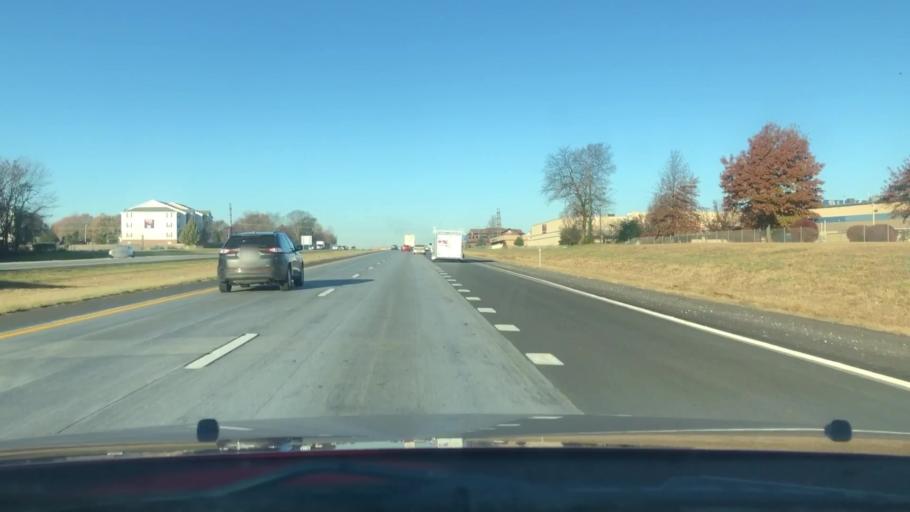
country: US
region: Missouri
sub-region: Greene County
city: Springfield
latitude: 37.1406
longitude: -93.2593
